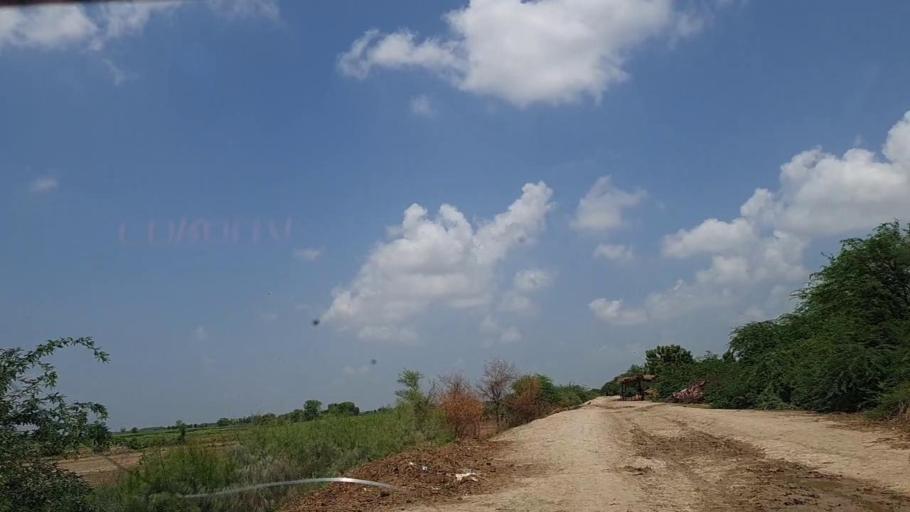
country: PK
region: Sindh
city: Tharu Shah
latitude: 26.9533
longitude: 68.0243
